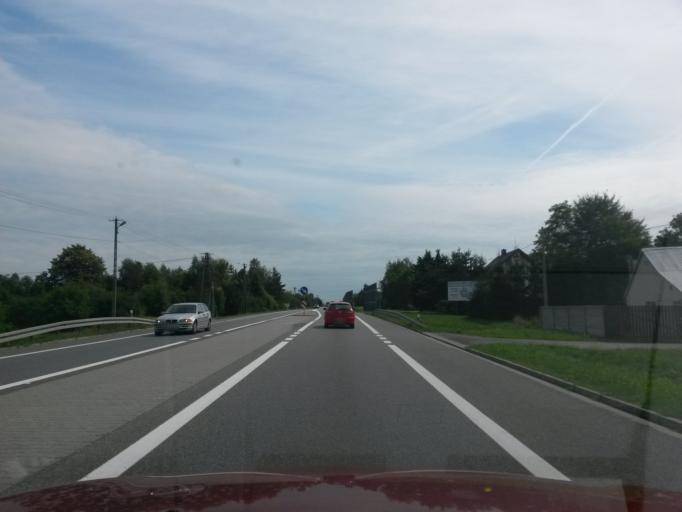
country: PL
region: Lesser Poland Voivodeship
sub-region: Powiat brzeski
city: Jasien
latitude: 49.9737
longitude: 20.5638
